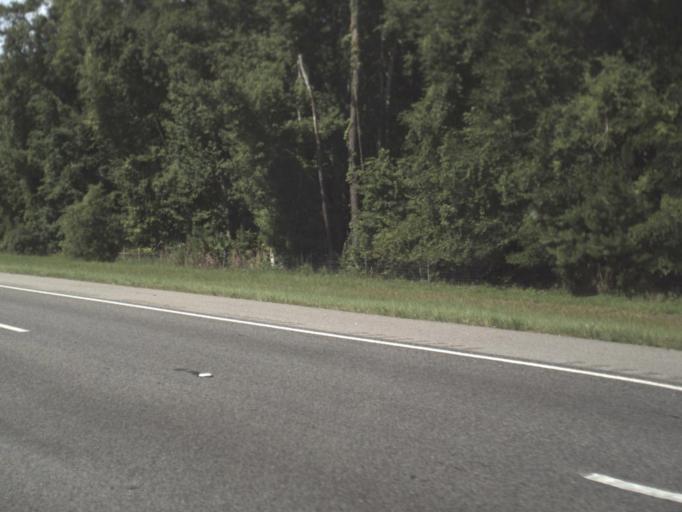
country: US
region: Florida
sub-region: Saint Johns County
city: Fruit Cove
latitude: 30.0786
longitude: -81.4986
